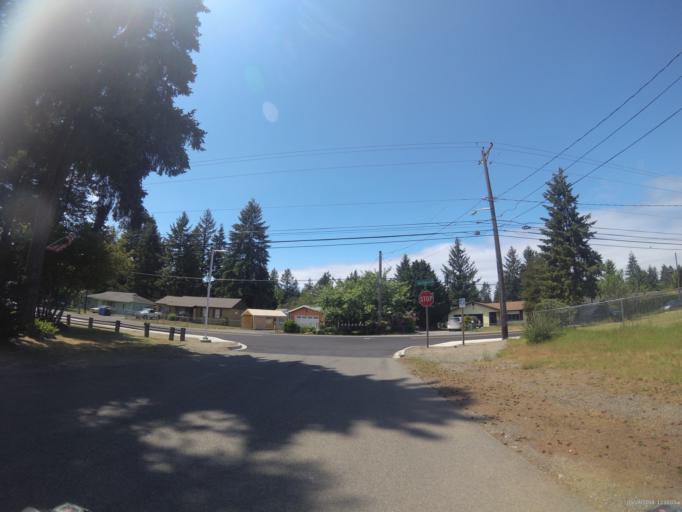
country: US
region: Washington
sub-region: Pierce County
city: Lakewood
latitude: 47.1825
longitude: -122.5233
